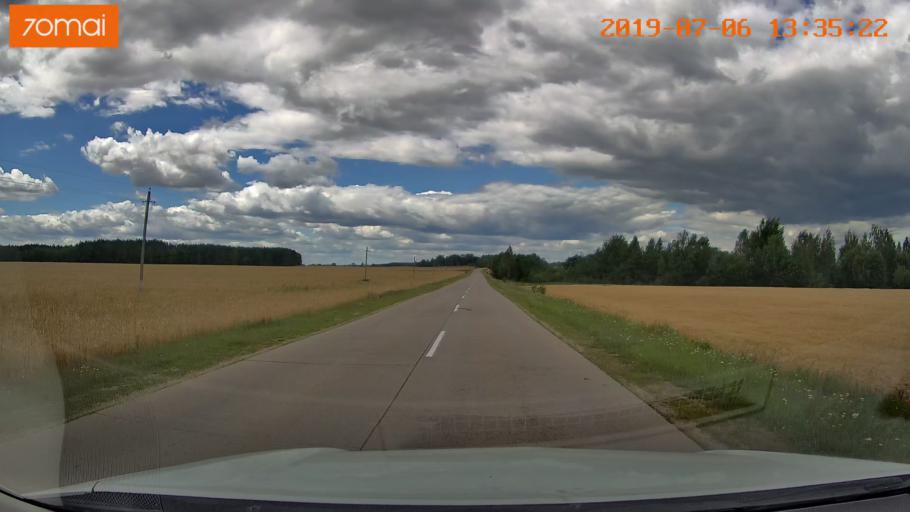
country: BY
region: Minsk
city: Enyerhyetykaw
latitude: 53.6818
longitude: 26.8819
